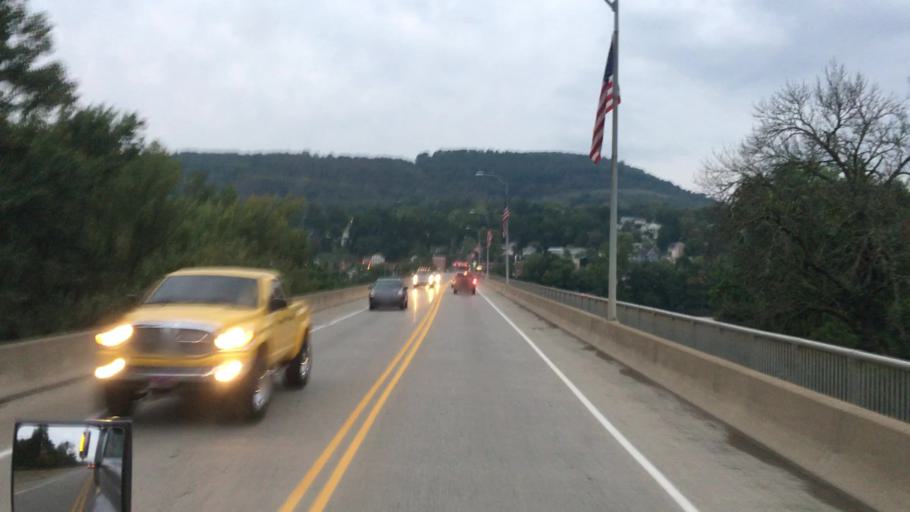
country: US
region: Pennsylvania
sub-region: Bradford County
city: Towanda
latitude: 41.7625
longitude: -76.4364
